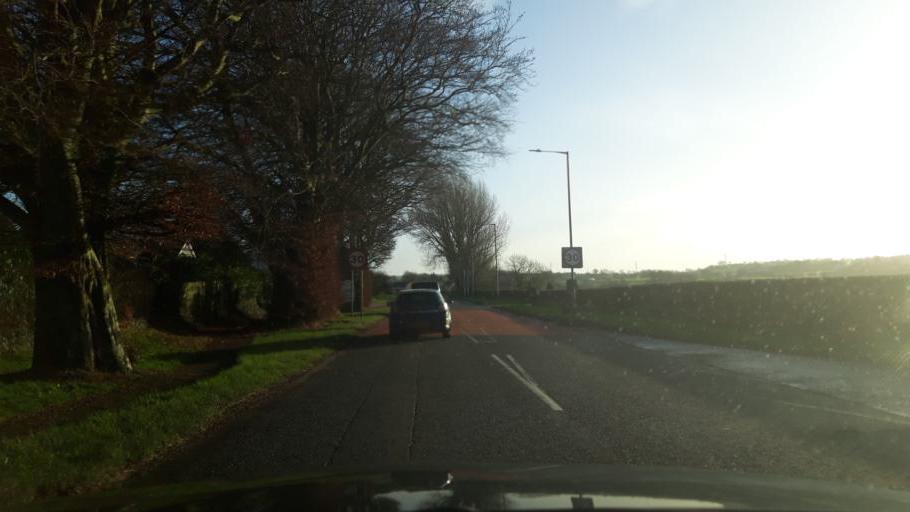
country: GB
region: Northern Ireland
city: Maghera
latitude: 54.7734
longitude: -6.6776
